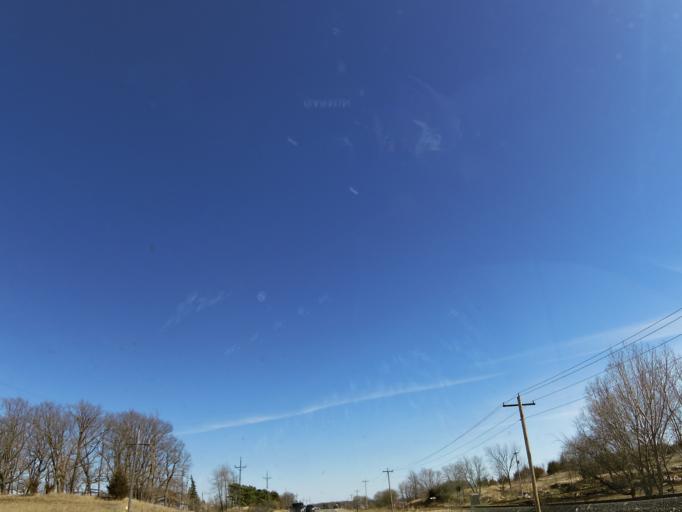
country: US
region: Minnesota
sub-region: Wright County
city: Annandale
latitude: 45.2433
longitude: -94.0705
